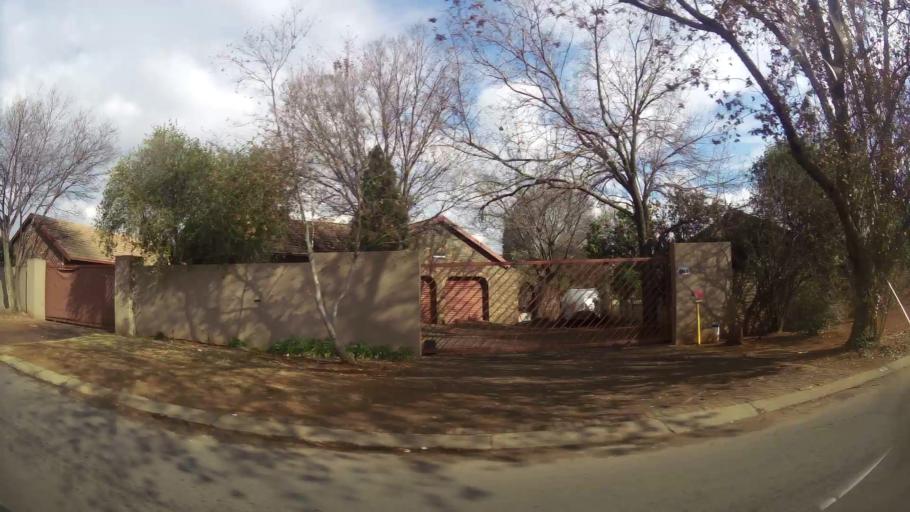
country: ZA
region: Gauteng
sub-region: Sedibeng District Municipality
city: Meyerton
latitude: -26.5544
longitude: 28.0321
